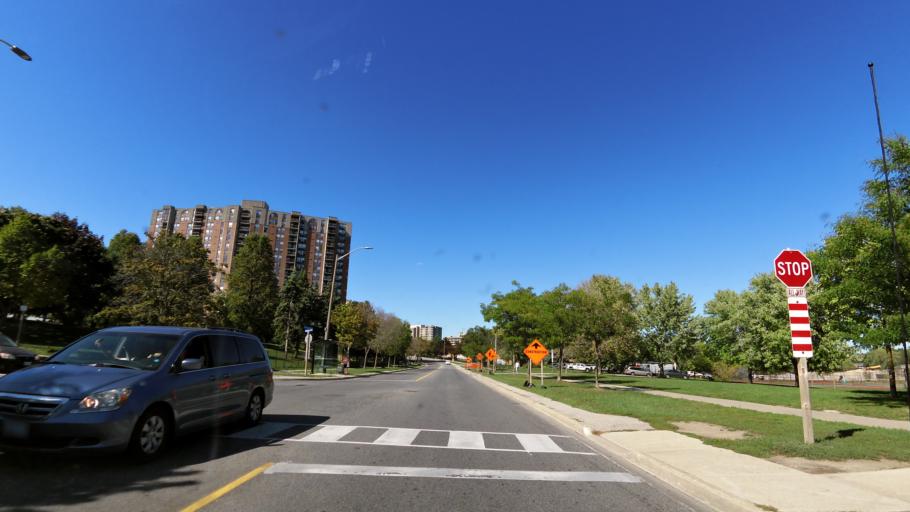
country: CA
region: Ontario
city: Mississauga
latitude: 43.5885
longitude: -79.6242
